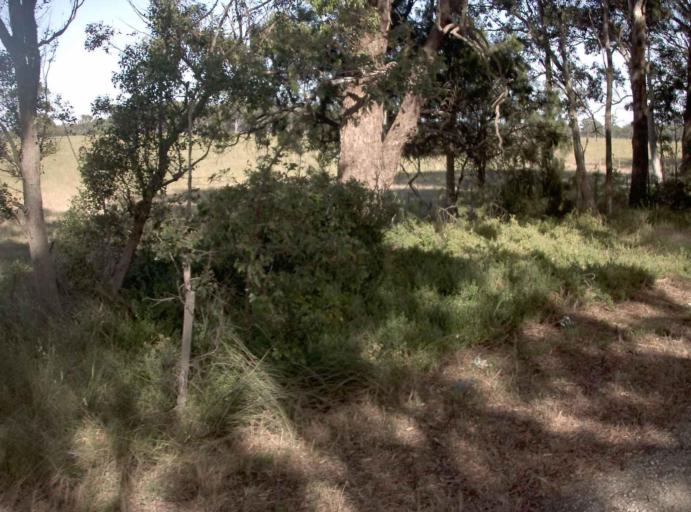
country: AU
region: Victoria
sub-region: East Gippsland
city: Lakes Entrance
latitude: -37.8084
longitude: 147.8430
